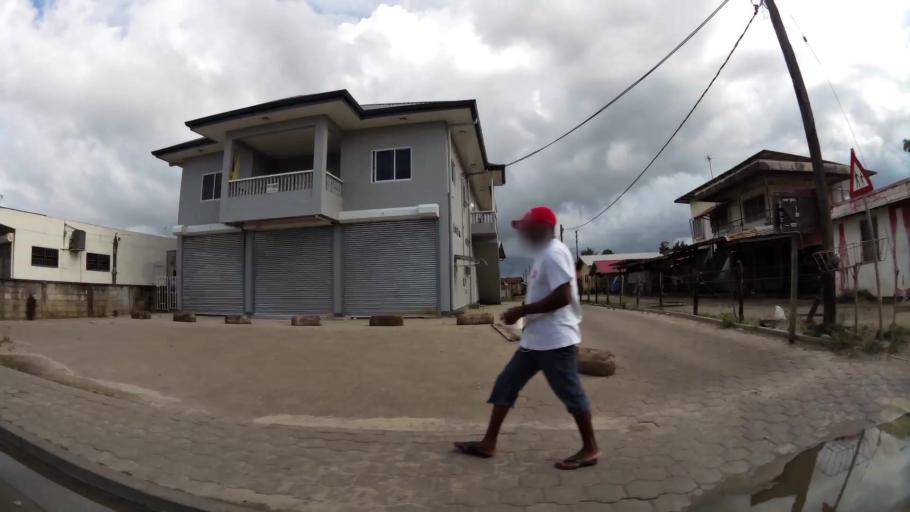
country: SR
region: Paramaribo
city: Paramaribo
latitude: 5.8464
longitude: -55.2309
